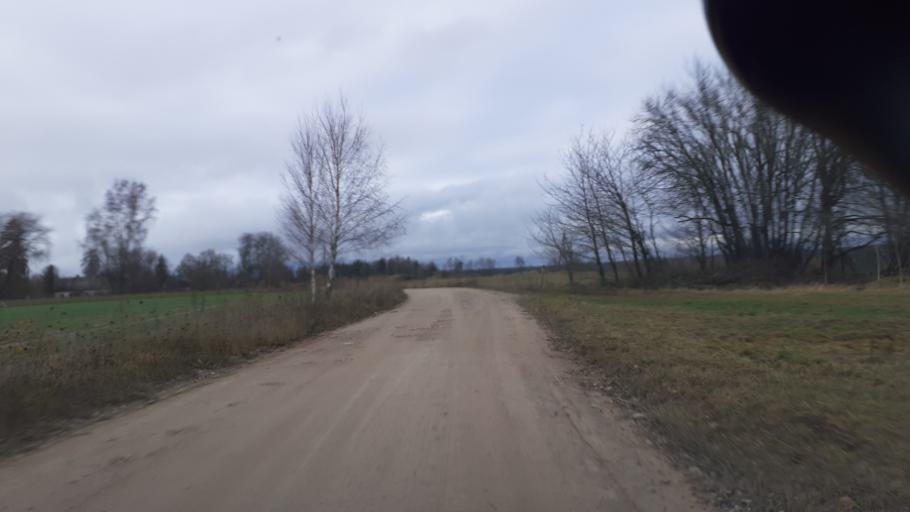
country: LV
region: Kuldigas Rajons
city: Kuldiga
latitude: 57.0435
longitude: 21.8719
